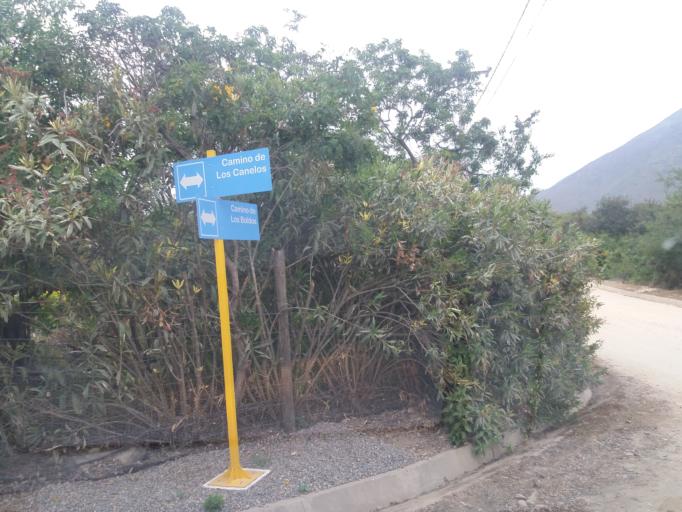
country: CL
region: Valparaiso
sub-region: Provincia de Marga Marga
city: Limache
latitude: -33.0249
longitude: -71.1340
